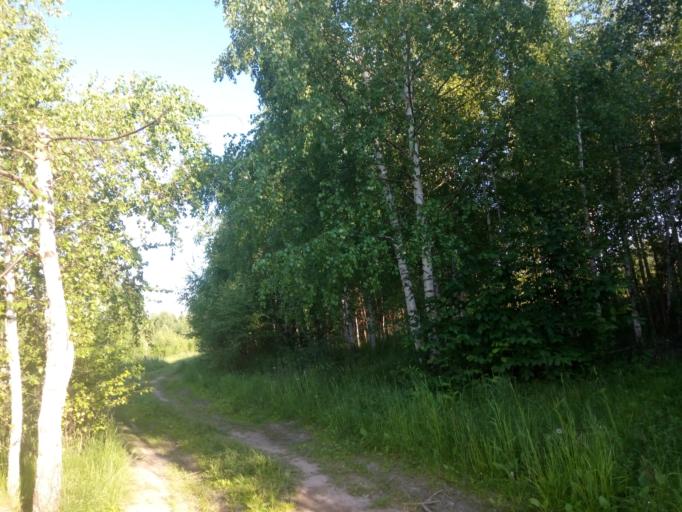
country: RU
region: Nizjnij Novgorod
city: Voskresenskoye
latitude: 56.7752
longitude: 45.5519
